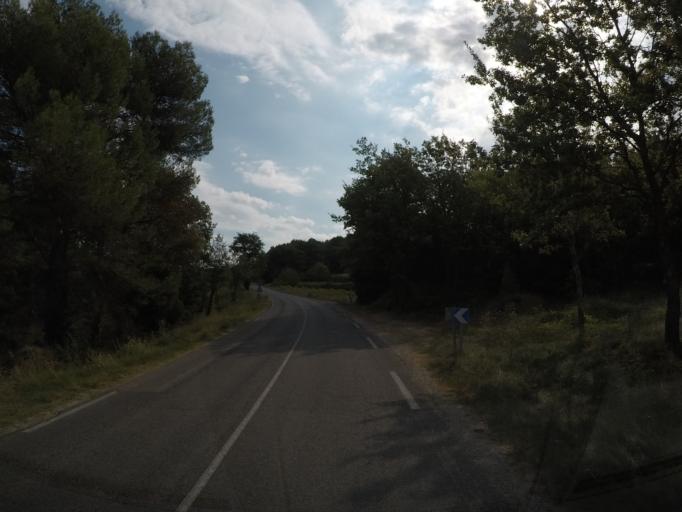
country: FR
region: Provence-Alpes-Cote d'Azur
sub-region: Departement du Vaucluse
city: Ansouis
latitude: 43.7277
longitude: 5.4911
